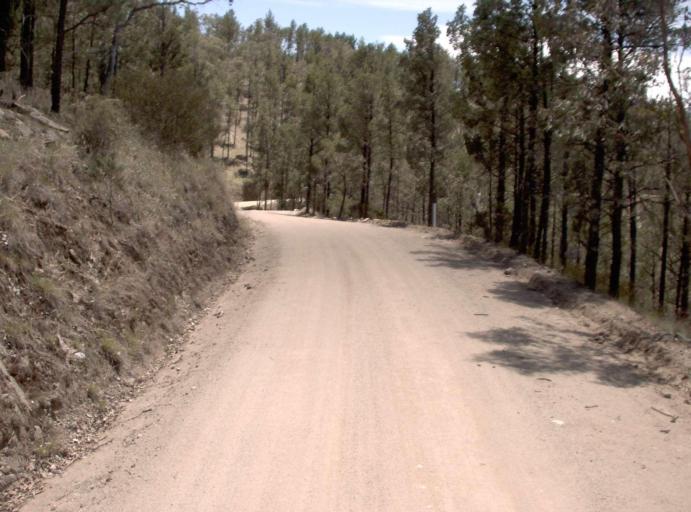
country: AU
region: New South Wales
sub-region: Snowy River
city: Jindabyne
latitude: -36.9076
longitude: 148.4160
